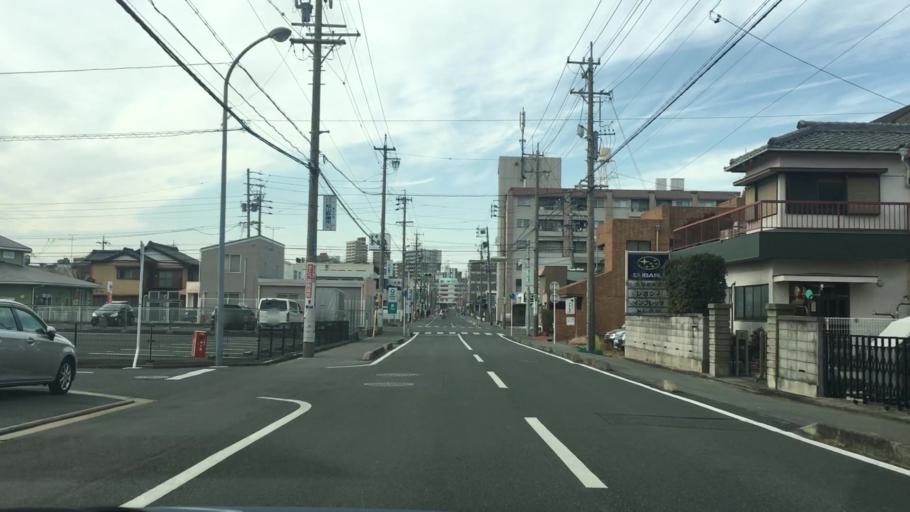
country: JP
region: Aichi
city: Toyohashi
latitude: 34.7595
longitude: 137.3979
